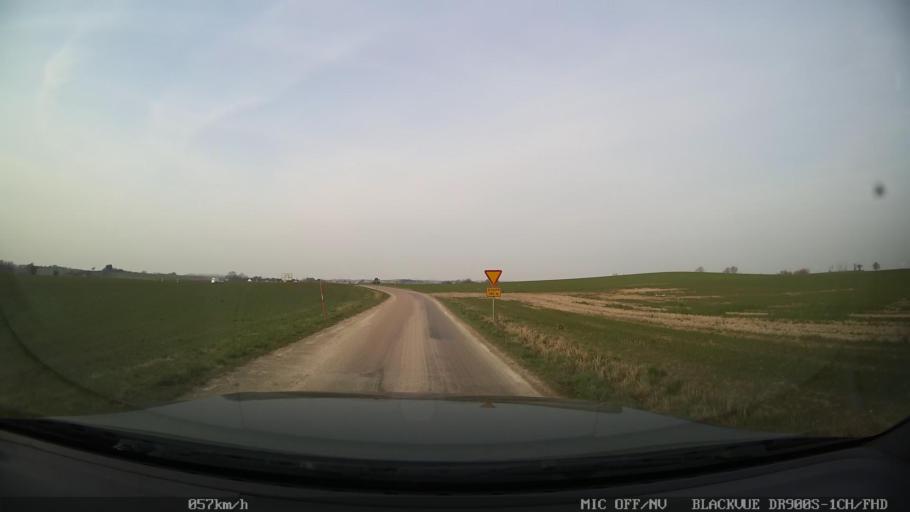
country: SE
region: Skane
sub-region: Ystads Kommun
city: Ystad
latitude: 55.4742
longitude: 13.8006
